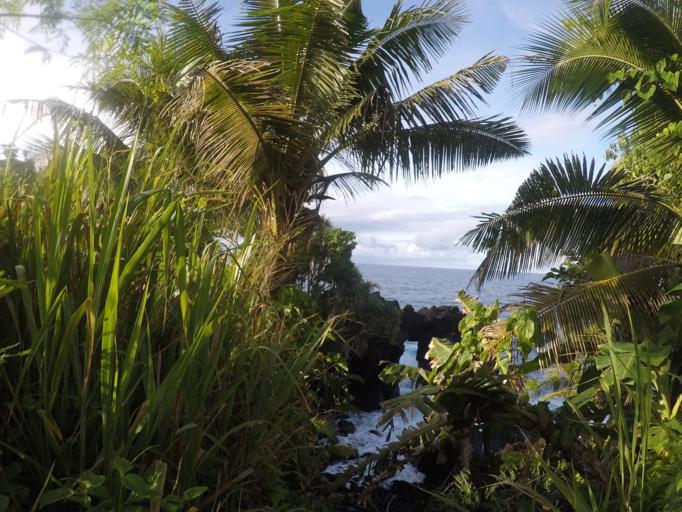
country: WS
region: Vaisigano
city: Asau
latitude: -13.6054
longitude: -172.7116
